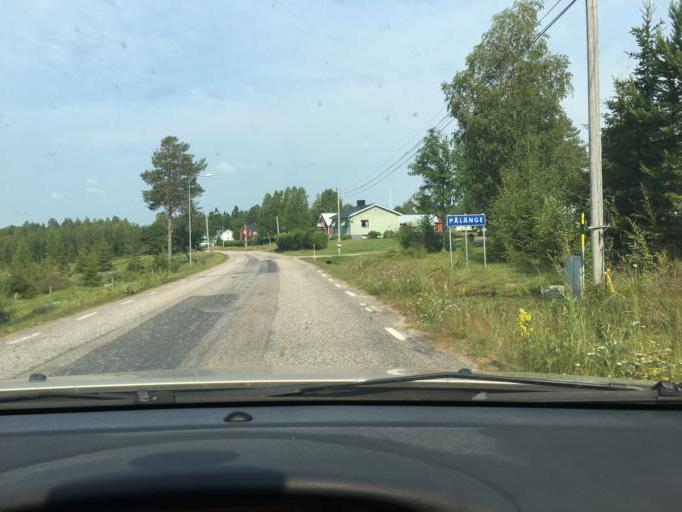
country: SE
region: Norrbotten
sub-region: Kalix Kommun
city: Rolfs
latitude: 65.8011
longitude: 22.9084
